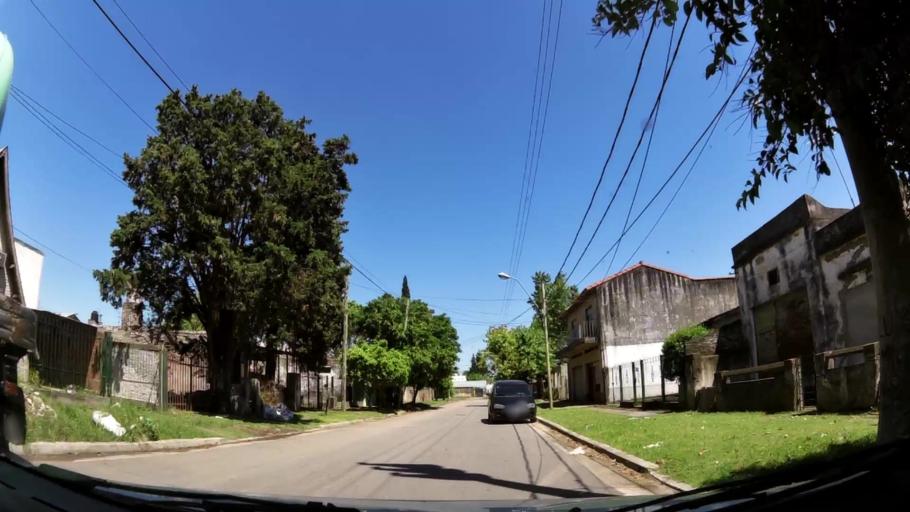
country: AR
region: Buenos Aires
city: Ituzaingo
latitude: -34.6852
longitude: -58.6663
